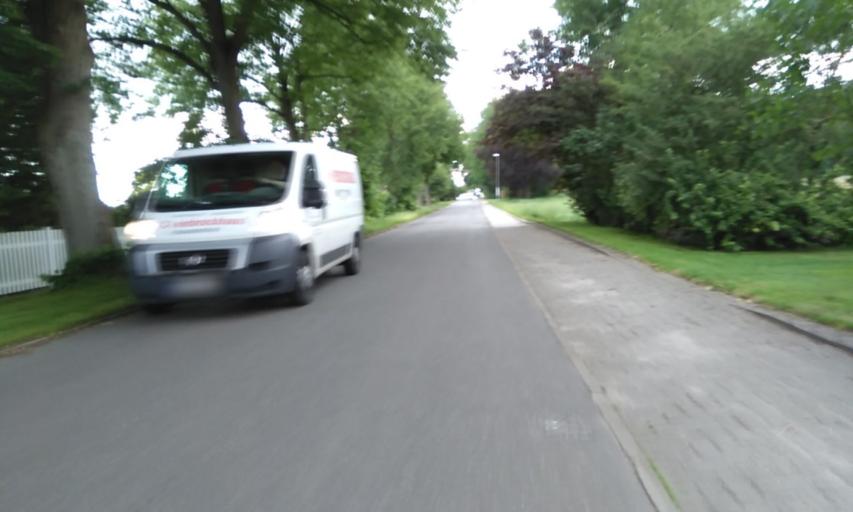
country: DE
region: Lower Saxony
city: Sauensiek
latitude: 53.3794
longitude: 9.5999
